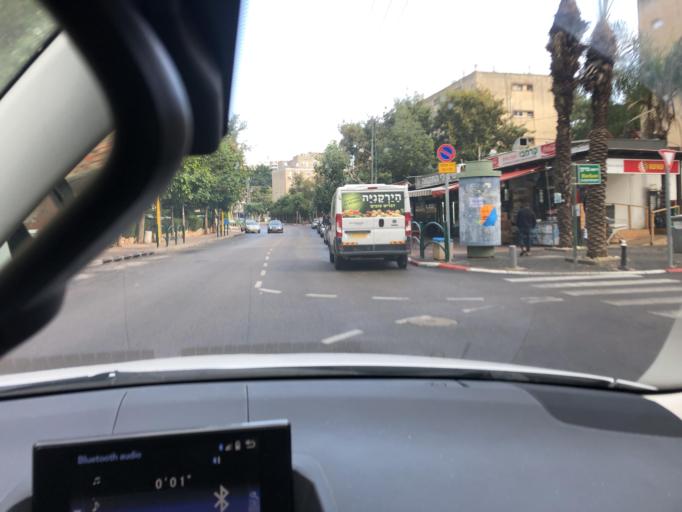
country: IL
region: Central District
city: Ganne Tiqwa
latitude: 32.0592
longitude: 34.8694
